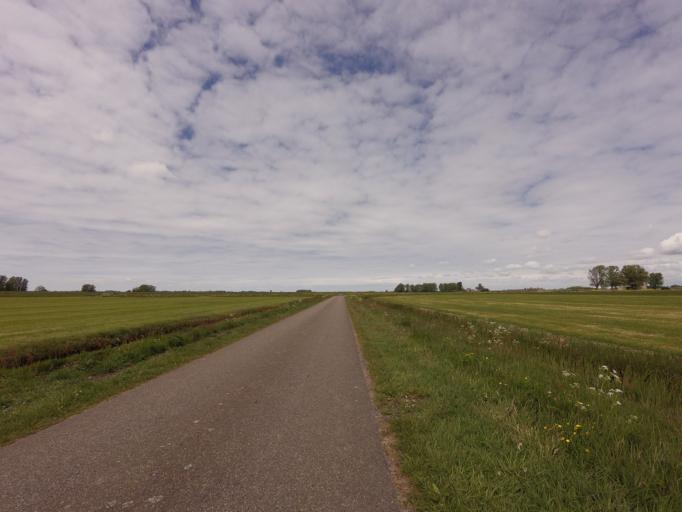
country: NL
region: Friesland
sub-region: Sudwest Fryslan
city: Koudum
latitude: 52.9071
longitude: 5.5016
